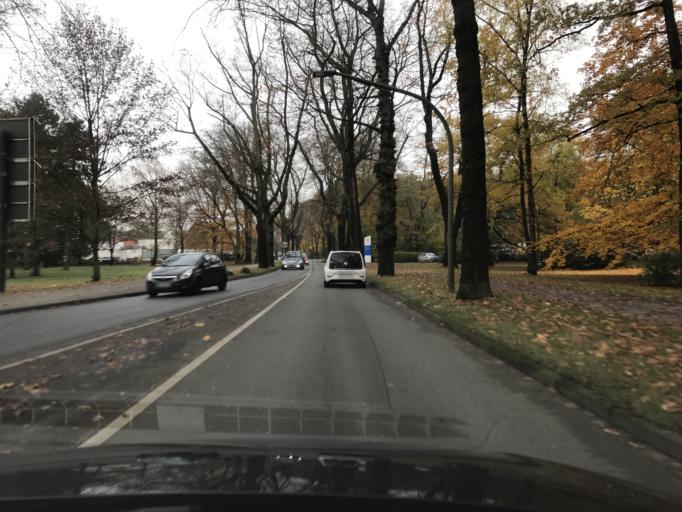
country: DE
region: North Rhine-Westphalia
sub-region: Regierungsbezirk Arnsberg
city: Hamm
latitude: 51.6897
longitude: 7.8419
